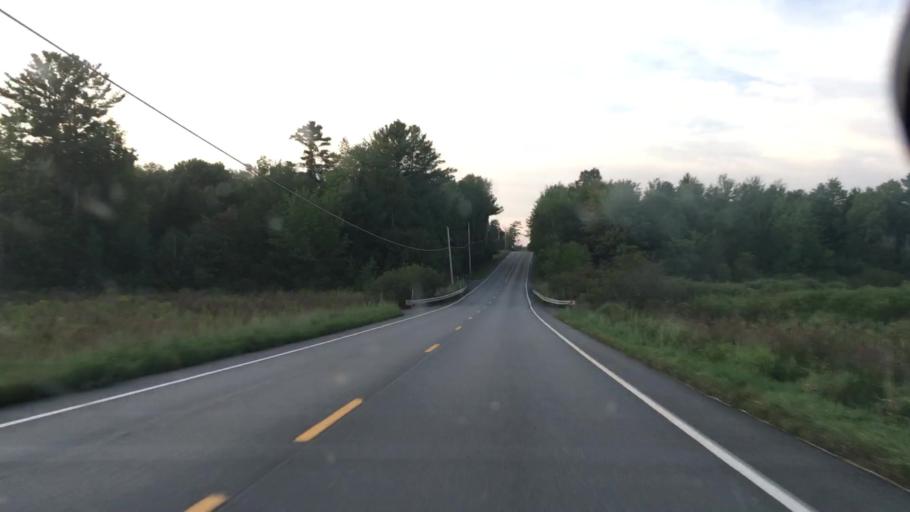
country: US
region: Maine
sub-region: Penobscot County
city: Hermon
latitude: 44.7502
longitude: -68.9697
